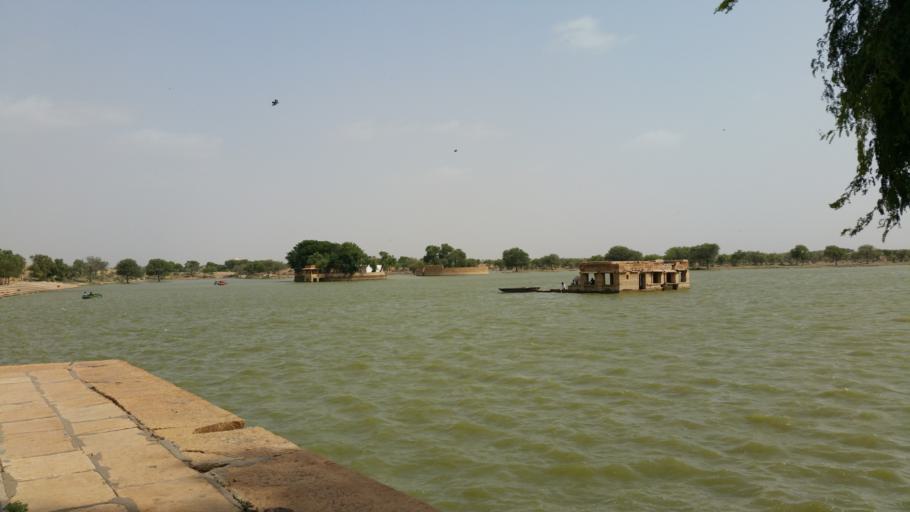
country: IN
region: Rajasthan
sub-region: Jaisalmer
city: Jaisalmer
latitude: 26.9096
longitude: 70.9222
